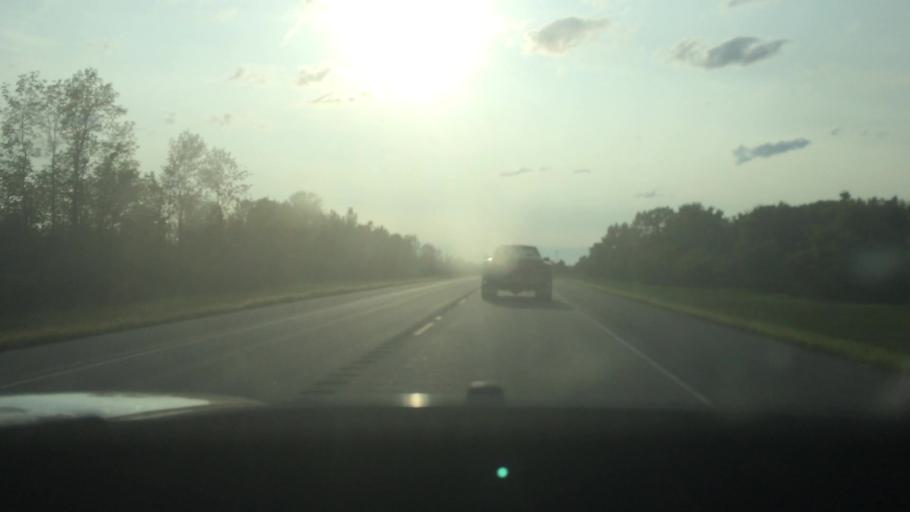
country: US
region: New York
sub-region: St. Lawrence County
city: Ogdensburg
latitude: 44.6791
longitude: -75.5087
